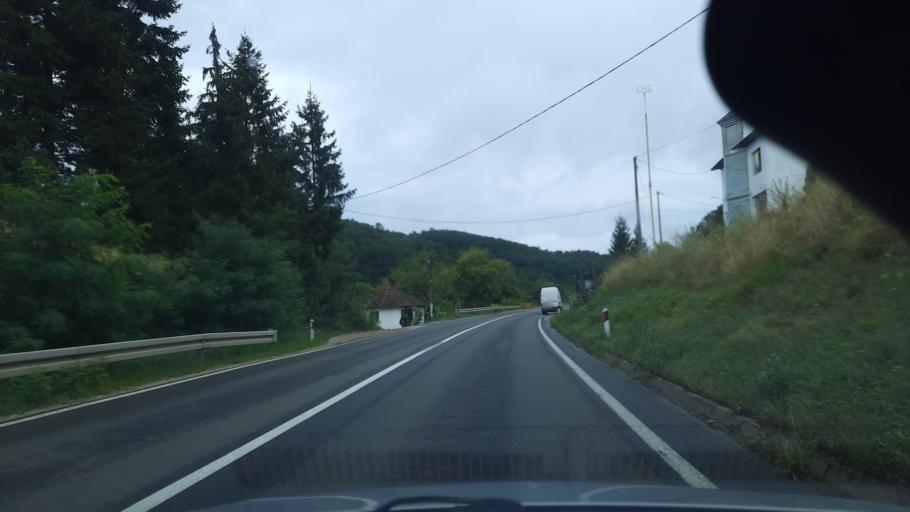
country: RS
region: Central Serbia
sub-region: Sumadijski Okrug
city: Knic
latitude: 43.9631
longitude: 20.8099
